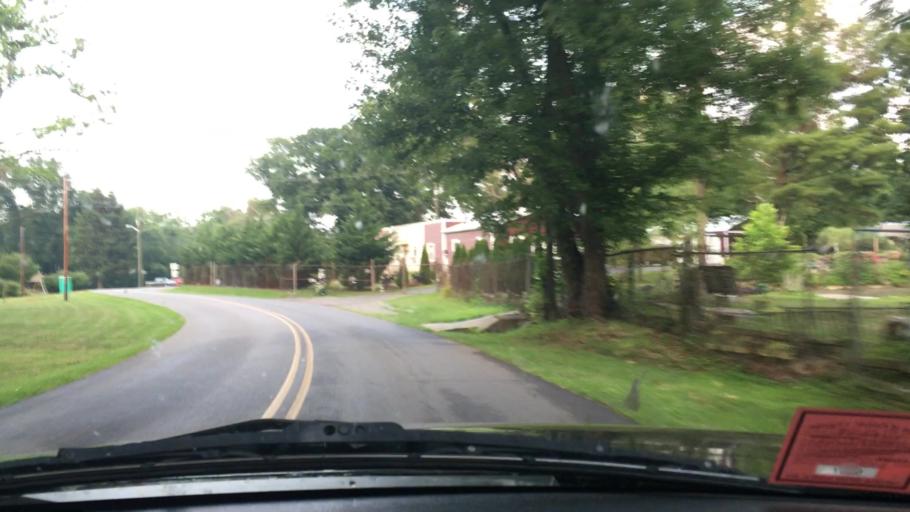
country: US
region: Virginia
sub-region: Pulaski County
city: Pulaski
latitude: 37.0433
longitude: -80.7632
